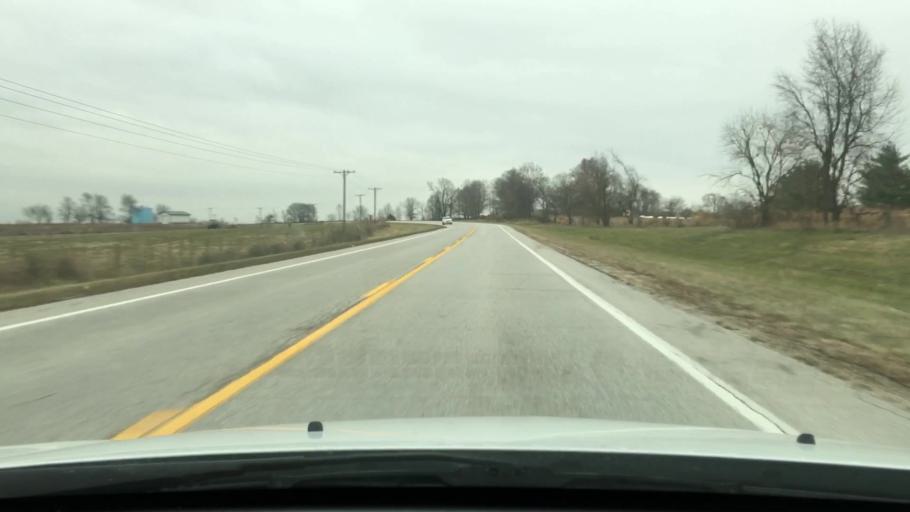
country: US
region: Illinois
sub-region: Pike County
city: Pittsfield
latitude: 39.5300
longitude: -90.9250
